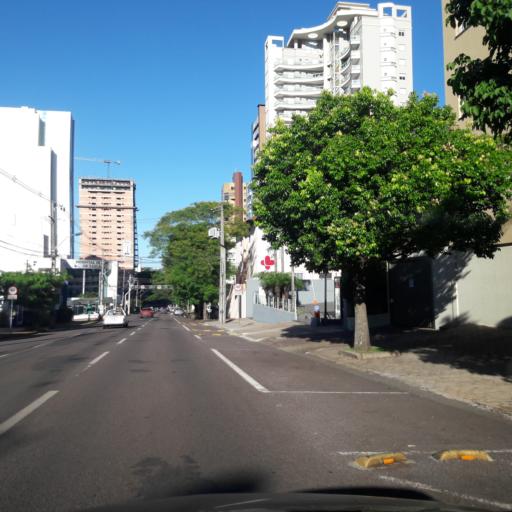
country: BR
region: Parana
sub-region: Cascavel
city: Cascavel
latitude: -24.9492
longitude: -53.4509
